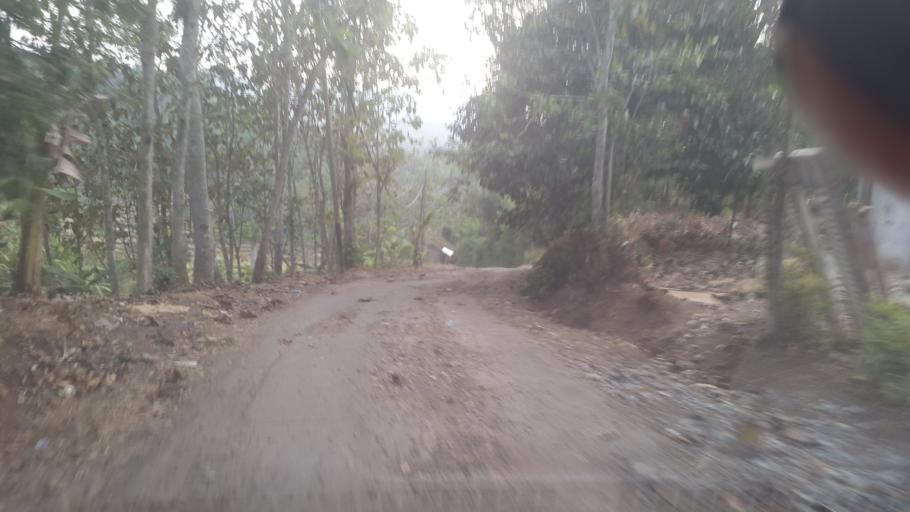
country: ID
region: West Java
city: Sukamaju
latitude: -7.0060
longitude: 106.8953
